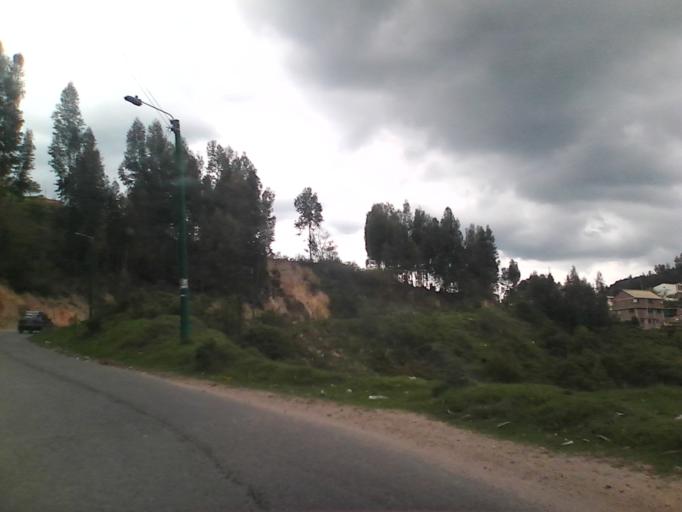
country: CO
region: Boyaca
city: Duitama
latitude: 5.8328
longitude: -73.0513
